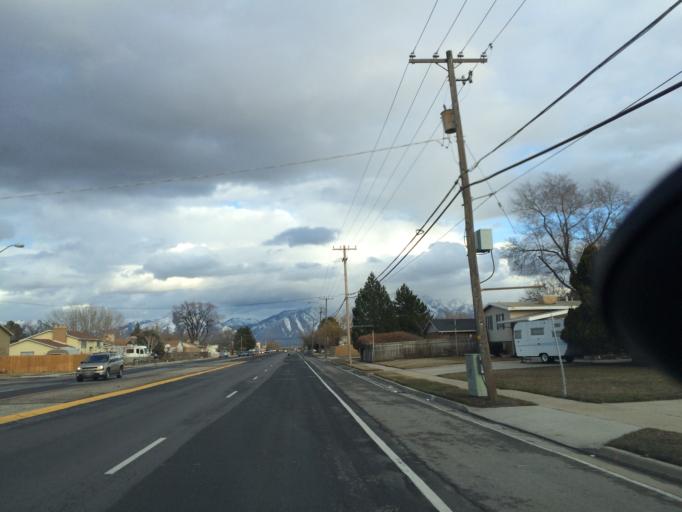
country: US
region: Utah
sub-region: Salt Lake County
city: Taylorsville
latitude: 40.6821
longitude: -111.9478
